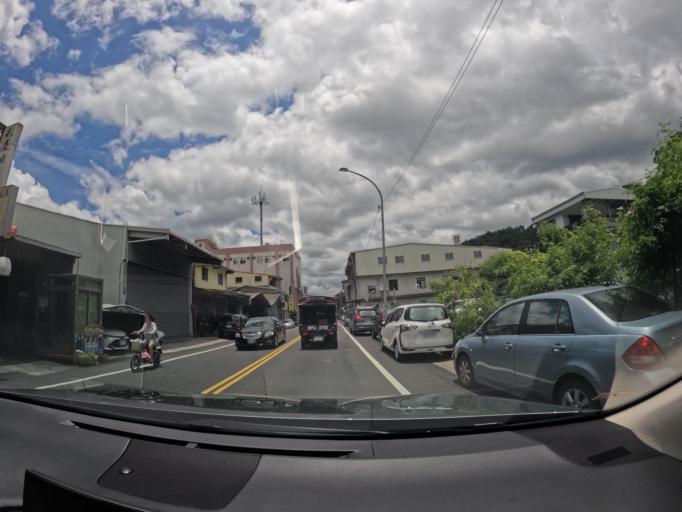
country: TW
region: Taiwan
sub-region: Miaoli
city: Miaoli
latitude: 24.6018
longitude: 120.9997
